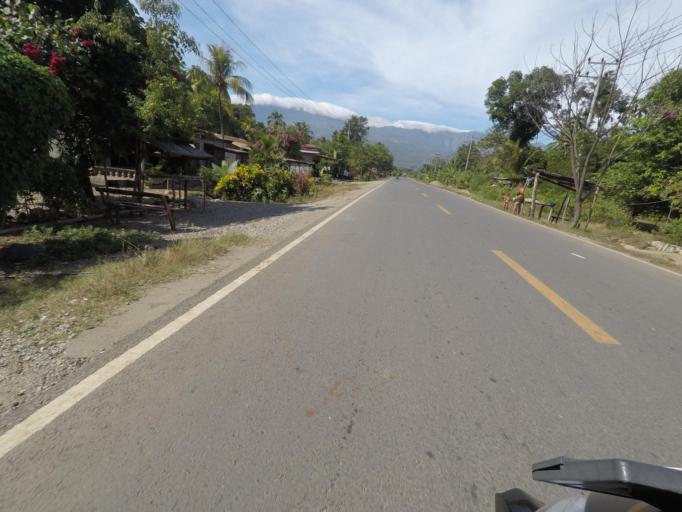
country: TL
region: Bobonaro
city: Maliana
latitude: -8.9686
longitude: 125.2179
